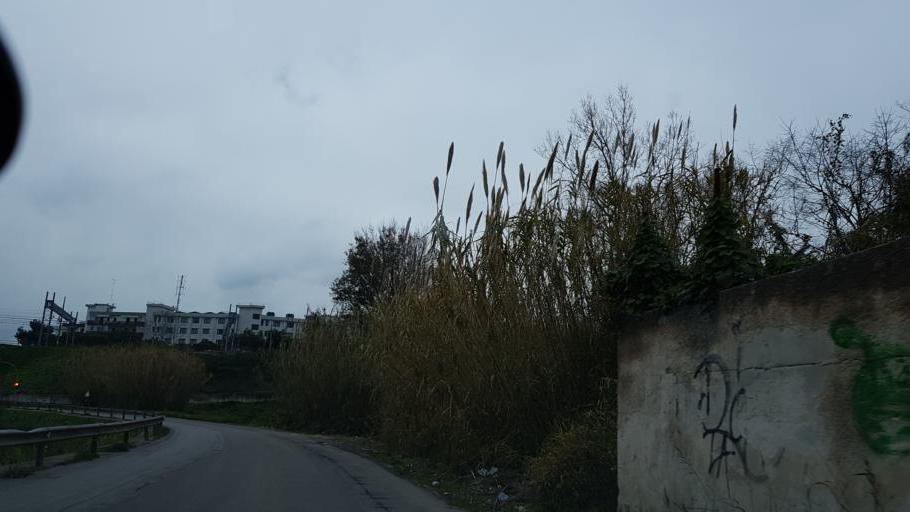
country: IT
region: Apulia
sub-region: Provincia di Brindisi
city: Brindisi
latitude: 40.6309
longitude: 17.9437
